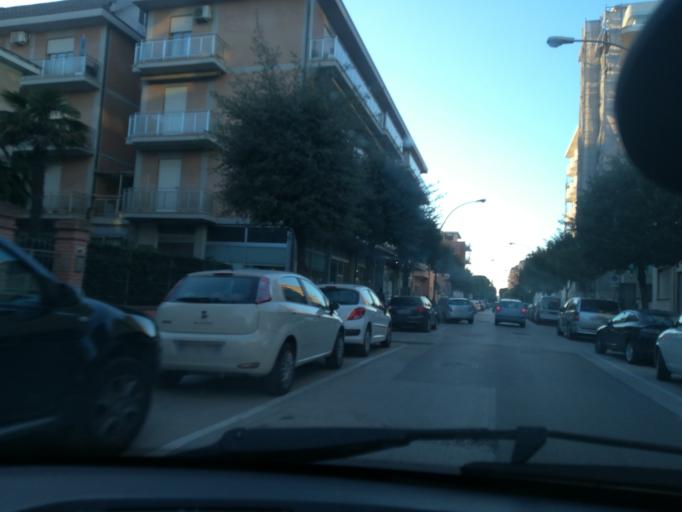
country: IT
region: The Marches
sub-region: Provincia di Macerata
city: Portocivitanova
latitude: 43.3024
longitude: 13.7358
